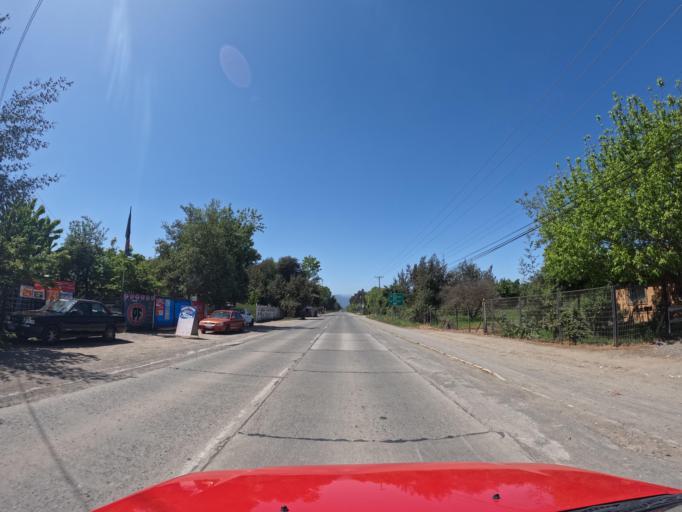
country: CL
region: Maule
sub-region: Provincia de Linares
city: Linares
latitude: -35.8318
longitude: -71.5245
